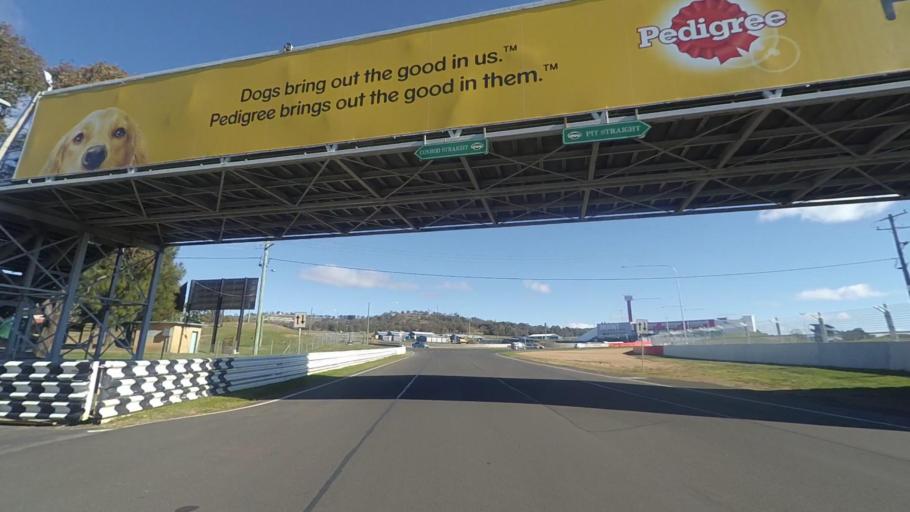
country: AU
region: New South Wales
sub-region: Bathurst Regional
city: Bathurst
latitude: -33.4392
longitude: 149.5619
